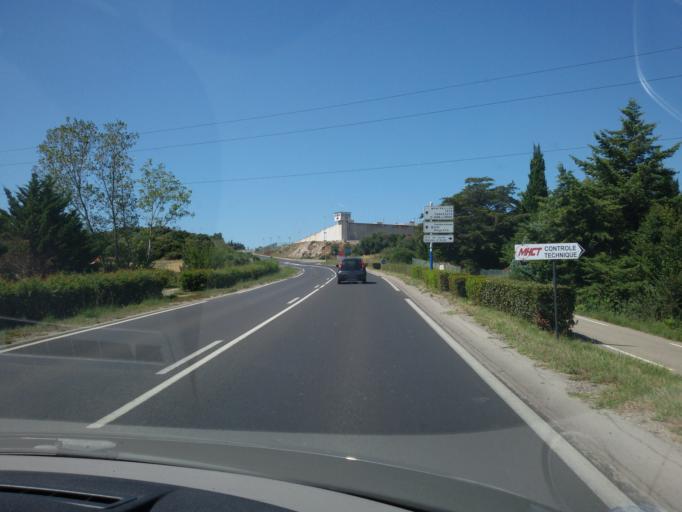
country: FR
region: Languedoc-Roussillon
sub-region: Departement de l'Herault
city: Saint-Jean-de-Vedas
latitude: 43.5447
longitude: 3.8312
